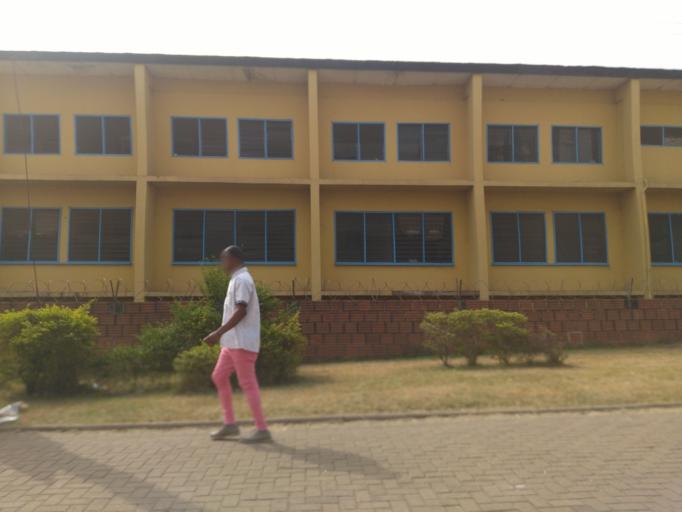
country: GH
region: Ashanti
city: Kumasi
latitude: 6.6917
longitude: -1.6114
